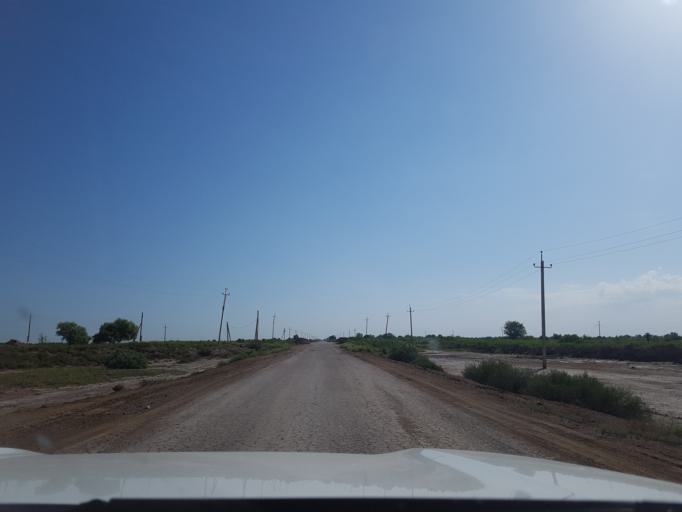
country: TM
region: Dasoguz
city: Koeneuergench
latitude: 42.0679
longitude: 58.8556
